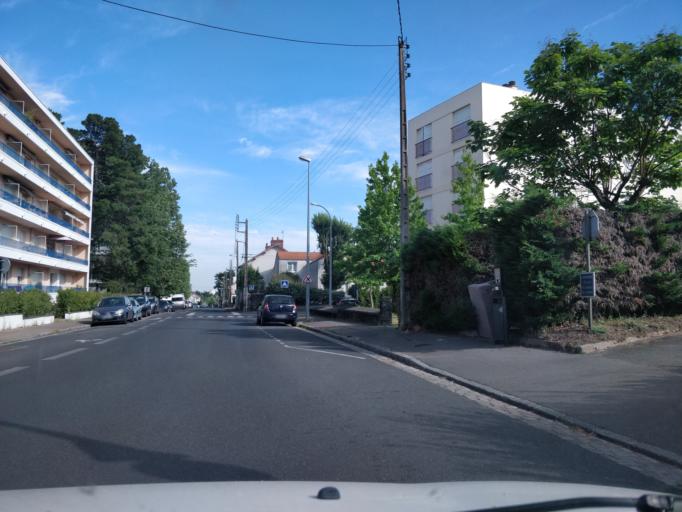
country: FR
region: Pays de la Loire
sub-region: Departement de la Loire-Atlantique
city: Nantes
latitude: 47.2390
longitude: -1.5276
